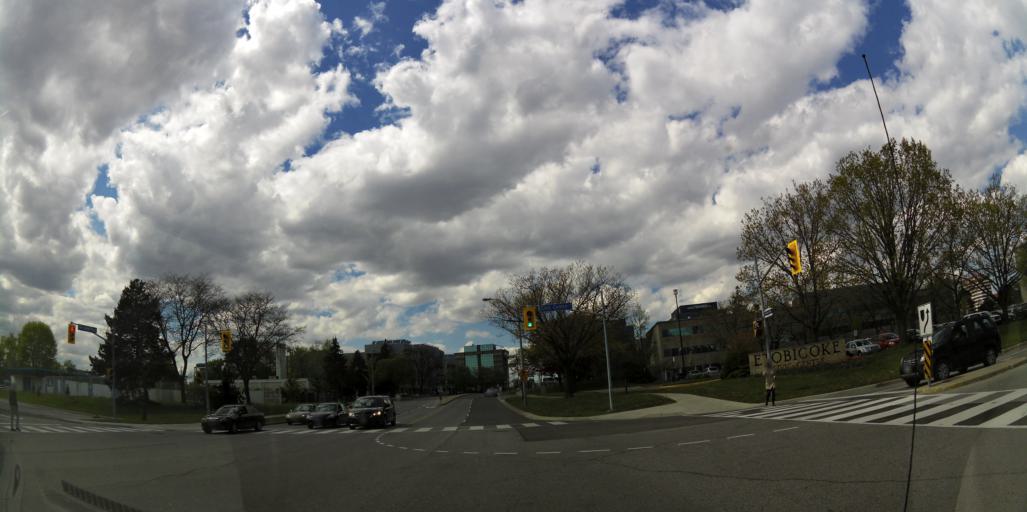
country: CA
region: Ontario
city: Etobicoke
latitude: 43.6422
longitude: -79.5659
